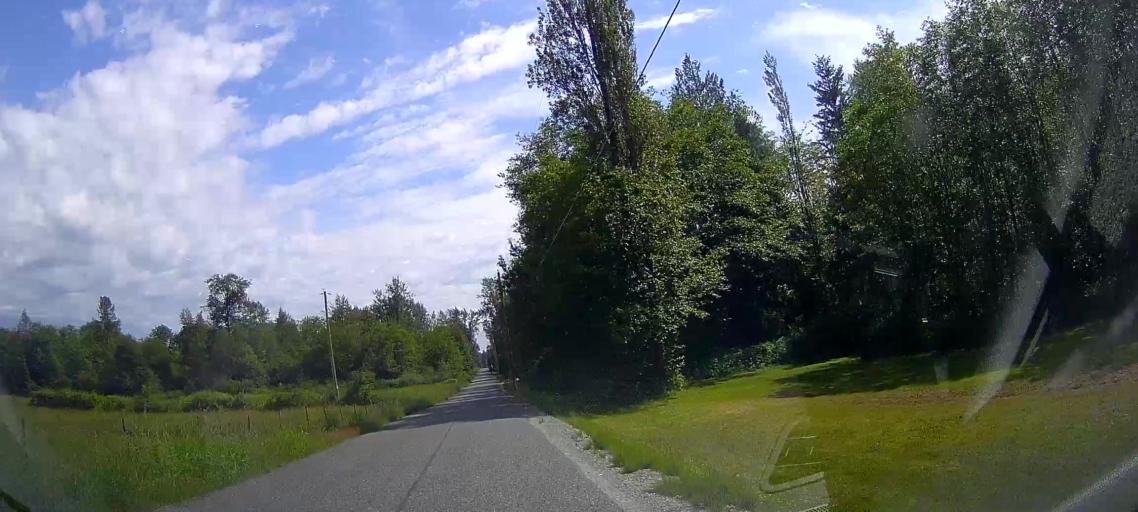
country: US
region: Washington
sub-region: Skagit County
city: Burlington
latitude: 48.5528
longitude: -122.3621
